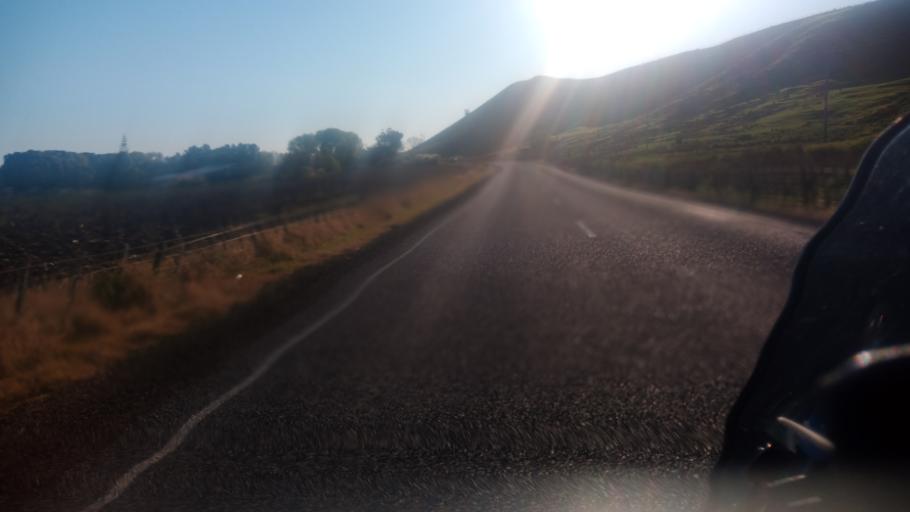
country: NZ
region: Hawke's Bay
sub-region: Wairoa District
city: Wairoa
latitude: -39.0475
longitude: 177.7655
